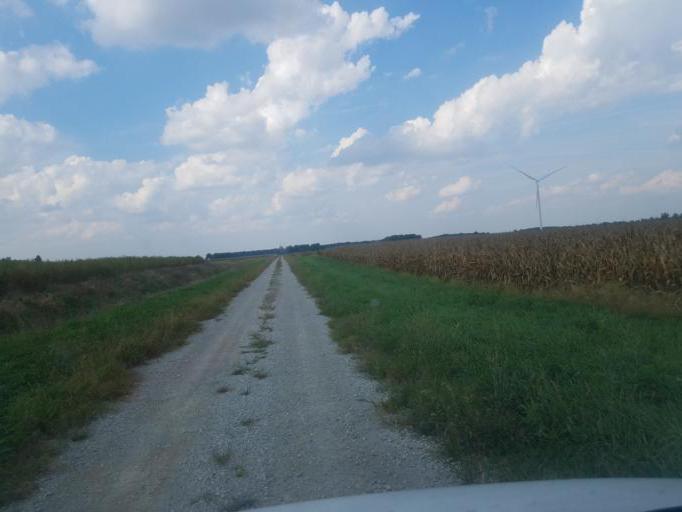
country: US
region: Ohio
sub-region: Hancock County
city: Arlington
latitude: 40.7968
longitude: -83.6898
